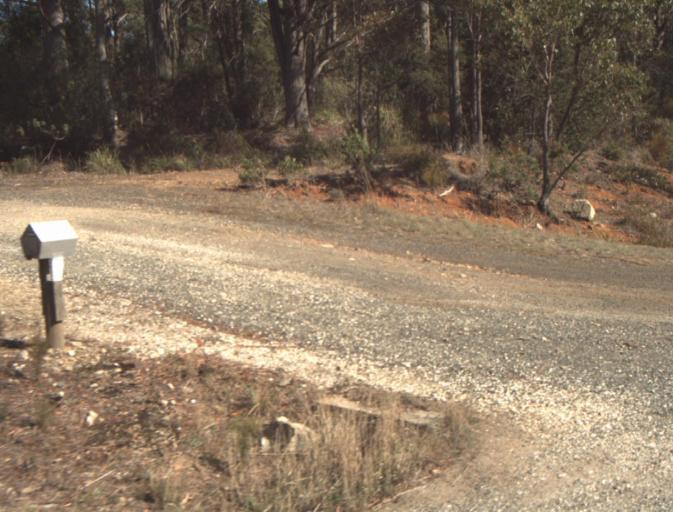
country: AU
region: Tasmania
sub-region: Launceston
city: Mayfield
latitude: -41.3370
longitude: 147.1688
